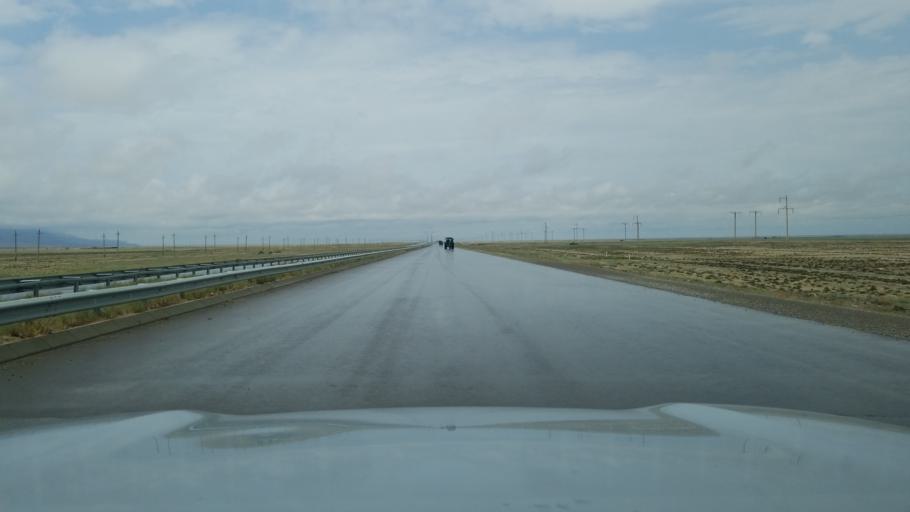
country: TM
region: Balkan
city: Gazanjyk
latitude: 39.1702
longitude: 55.8217
